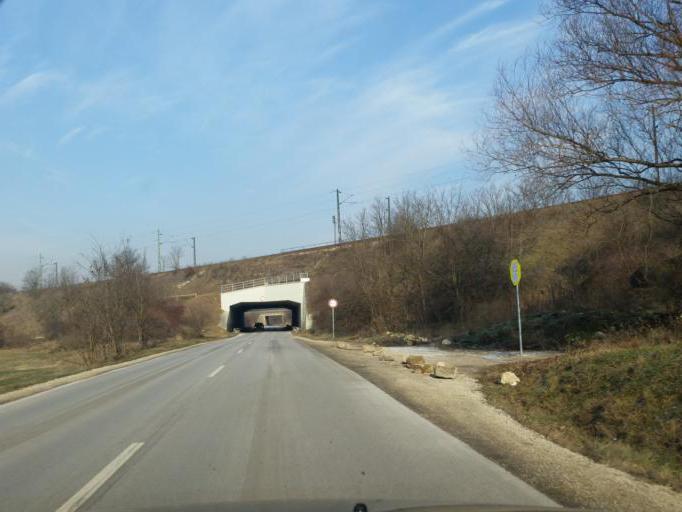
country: HU
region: Pest
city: Biatorbagy
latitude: 47.4868
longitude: 18.8260
